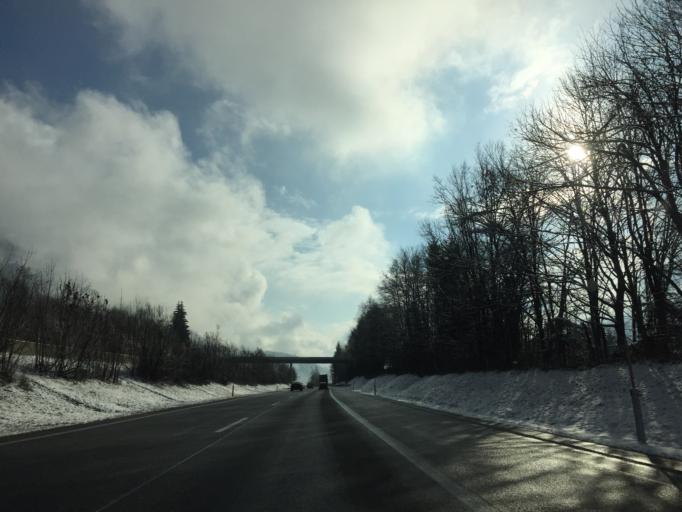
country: AT
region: Salzburg
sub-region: Politischer Bezirk Sankt Johann im Pongau
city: Werfenweng
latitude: 47.4351
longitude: 13.2509
